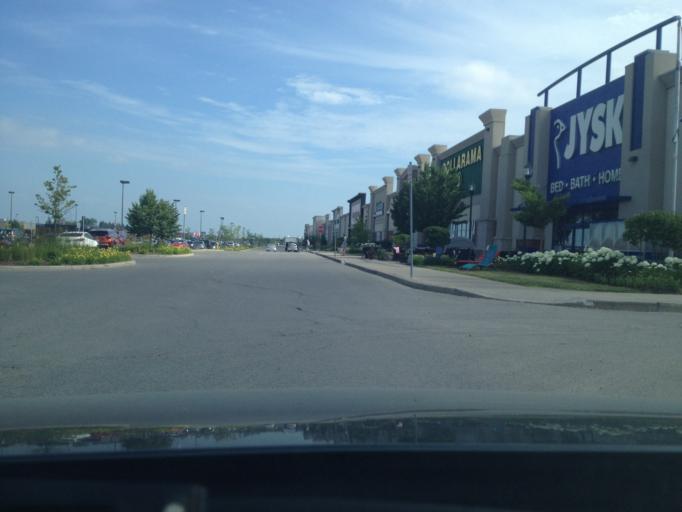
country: CA
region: Ontario
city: London
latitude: 42.9369
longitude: -81.2834
